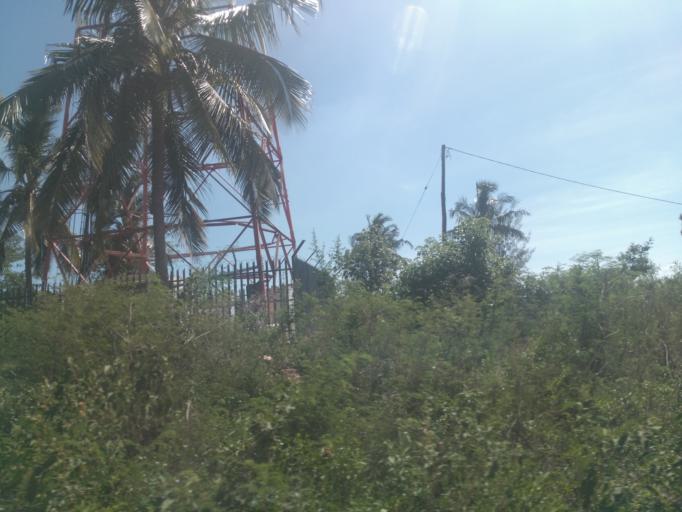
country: TZ
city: Kiwengwa
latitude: -5.9928
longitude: 39.3358
